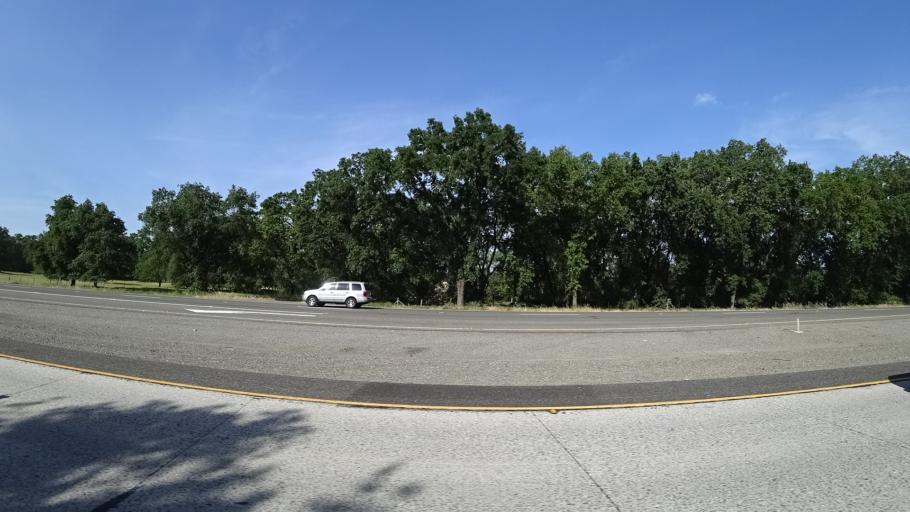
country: US
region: California
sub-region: Butte County
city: Durham
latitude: 39.6892
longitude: -121.7726
